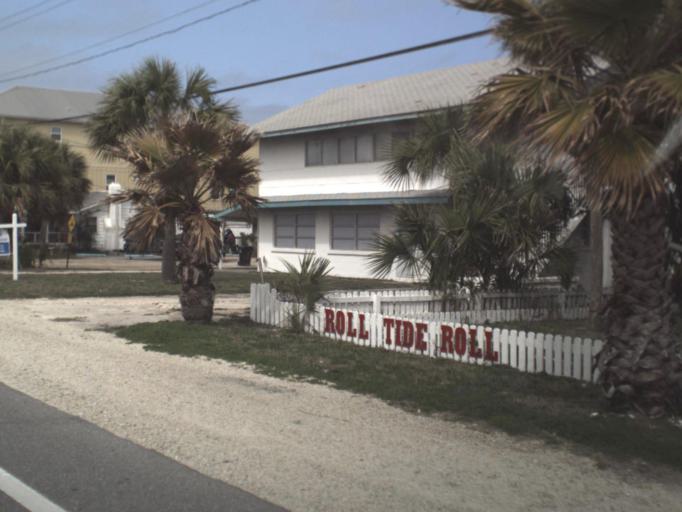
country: US
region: Florida
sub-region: Bay County
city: Panama City Beach
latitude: 30.1976
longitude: -85.8431
